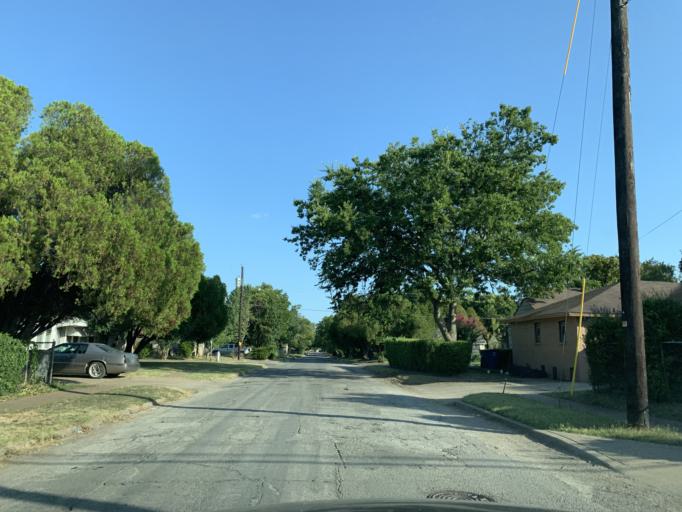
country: US
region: Texas
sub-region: Dallas County
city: Dallas
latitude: 32.7066
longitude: -96.7938
